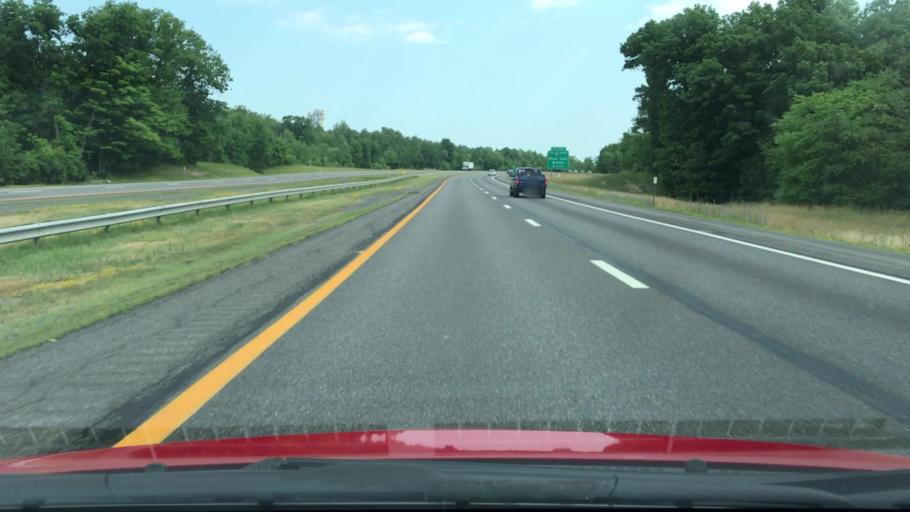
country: US
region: New York
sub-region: Albany County
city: Ravena
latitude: 42.4801
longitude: -73.8078
